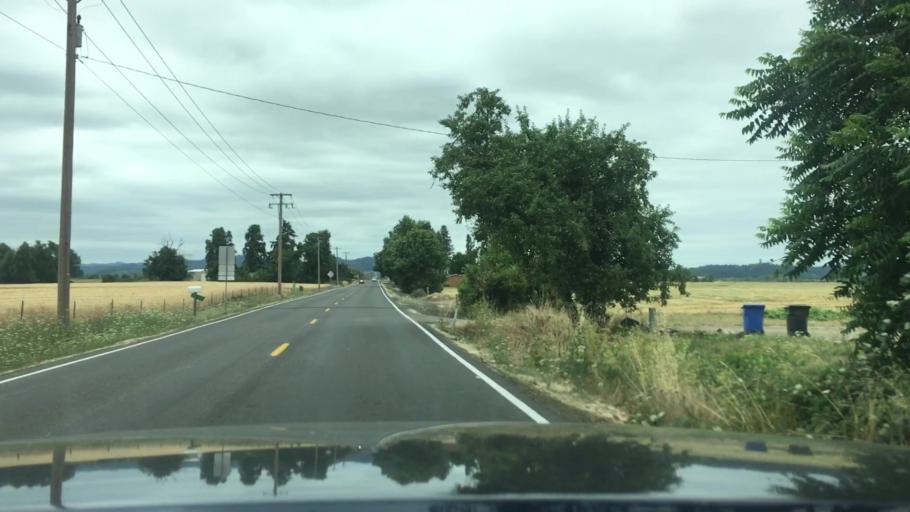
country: US
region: Oregon
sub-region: Lane County
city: Junction City
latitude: 44.1025
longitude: -123.2084
